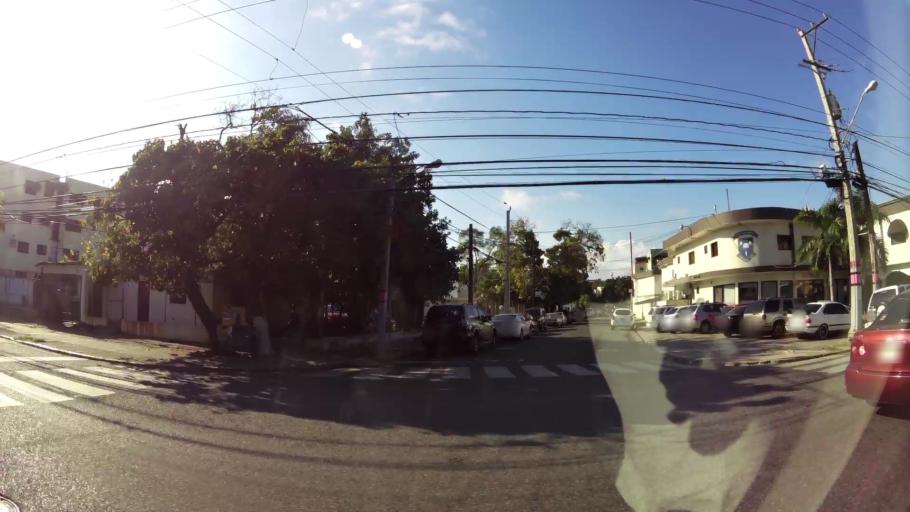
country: DO
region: Nacional
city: Bella Vista
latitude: 18.4477
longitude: -69.9323
